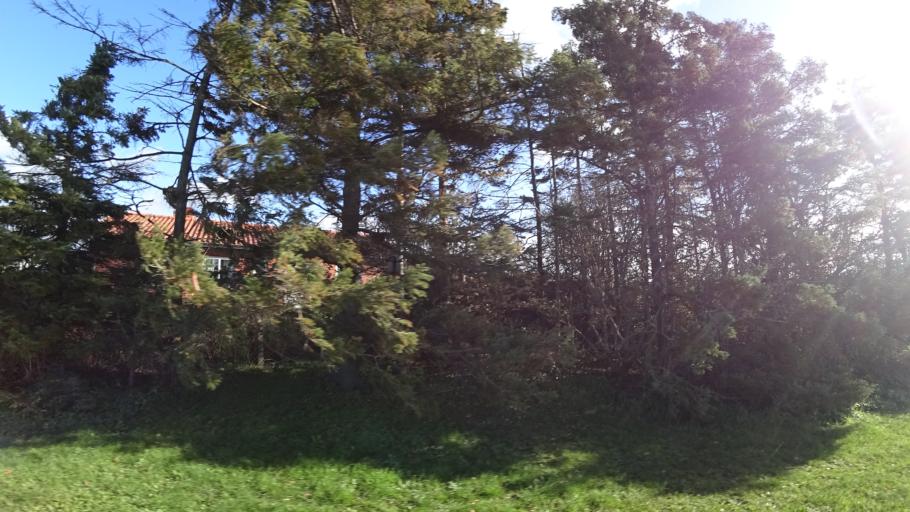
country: SE
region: Skane
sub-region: Staffanstorps Kommun
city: Hjaerup
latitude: 55.6886
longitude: 13.1443
